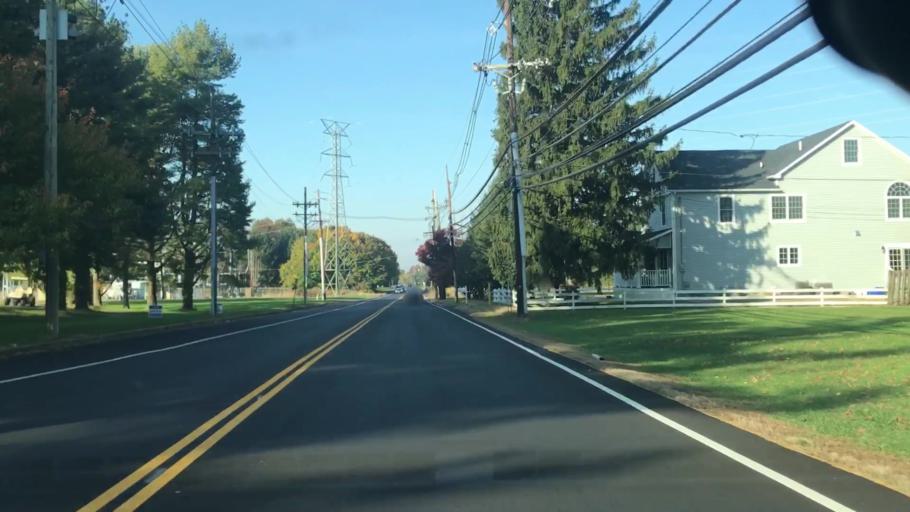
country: US
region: New Jersey
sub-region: Middlesex County
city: Princeton Meadows
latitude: 40.3368
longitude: -74.5663
